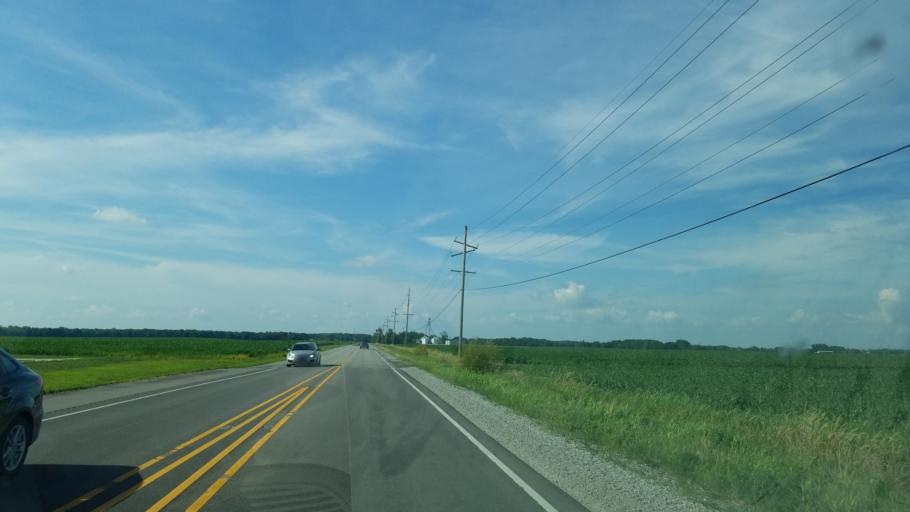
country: US
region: Illinois
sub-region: Saint Clair County
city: Scott Air Force Base
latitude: 38.5574
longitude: -89.8073
